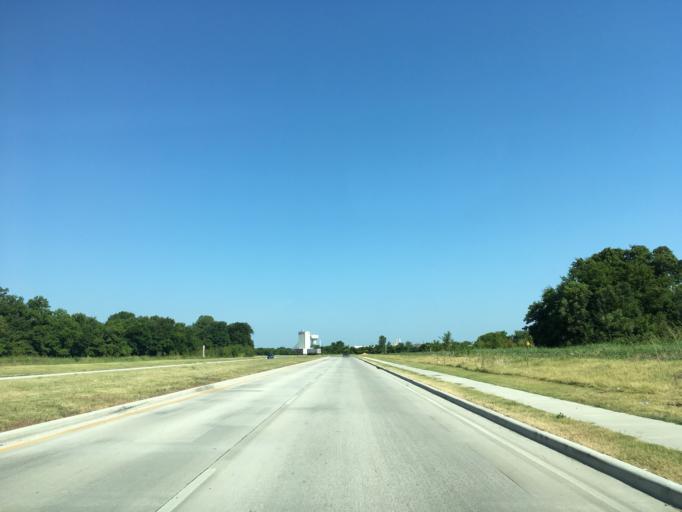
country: US
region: Texas
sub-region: Collin County
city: Fairview
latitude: 33.1683
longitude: -96.6033
